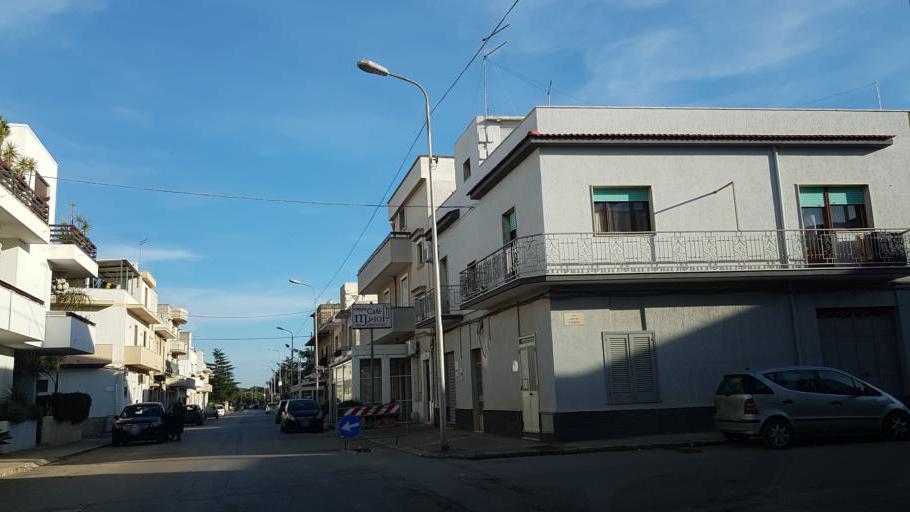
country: IT
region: Apulia
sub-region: Provincia di Brindisi
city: Carovigno
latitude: 40.7034
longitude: 17.6649
